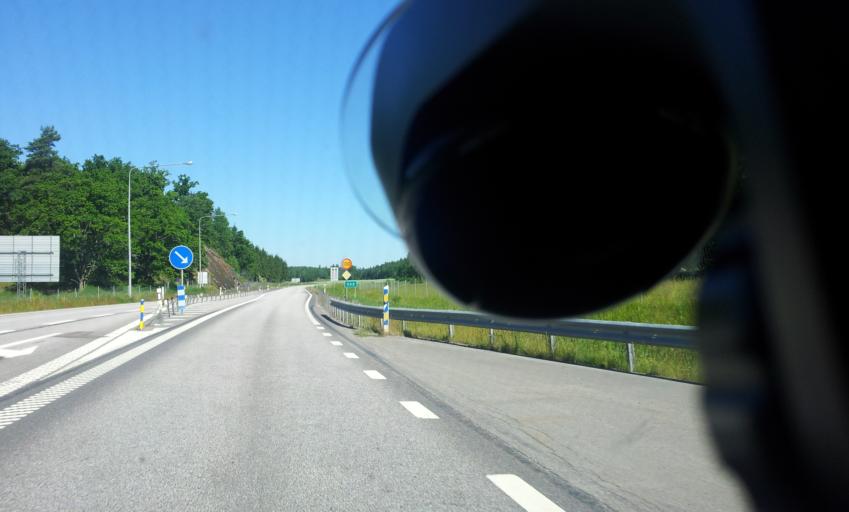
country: SE
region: OEstergoetland
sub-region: Valdemarsviks Kommun
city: Gusum
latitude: 58.3826
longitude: 16.4162
